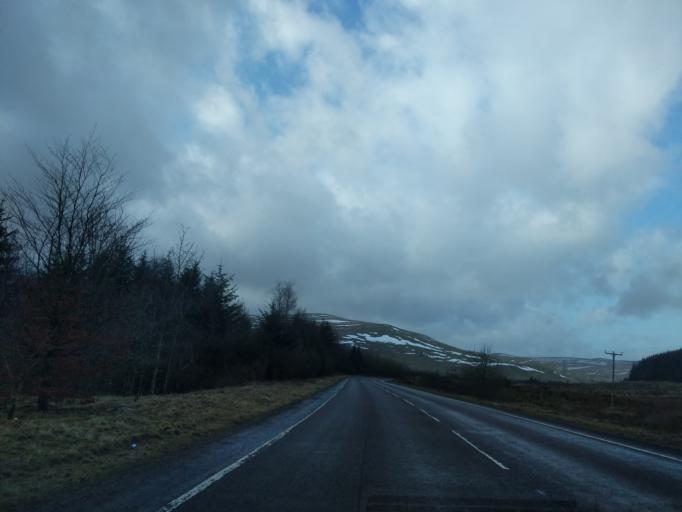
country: GB
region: Scotland
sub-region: Dumfries and Galloway
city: Moffat
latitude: 55.4299
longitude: -3.6231
